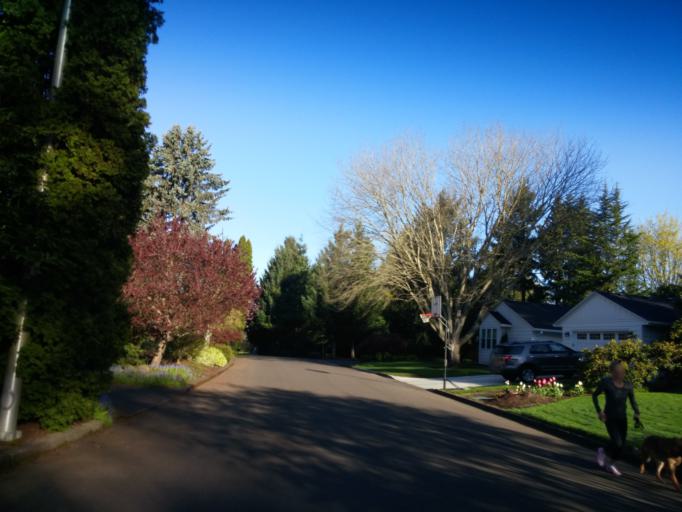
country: US
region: Oregon
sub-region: Washington County
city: Cedar Hills
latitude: 45.5114
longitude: -122.7911
